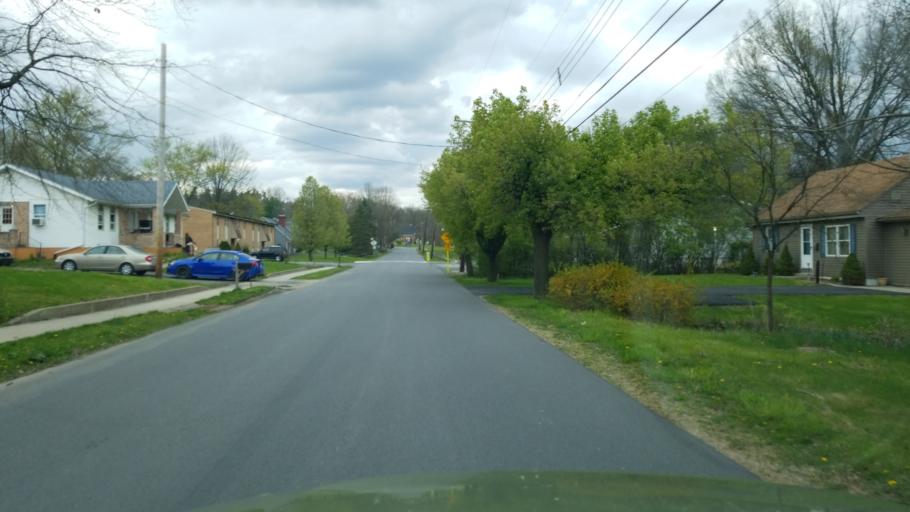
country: US
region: Pennsylvania
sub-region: Blair County
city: Hollidaysburg
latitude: 40.4376
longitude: -78.3997
